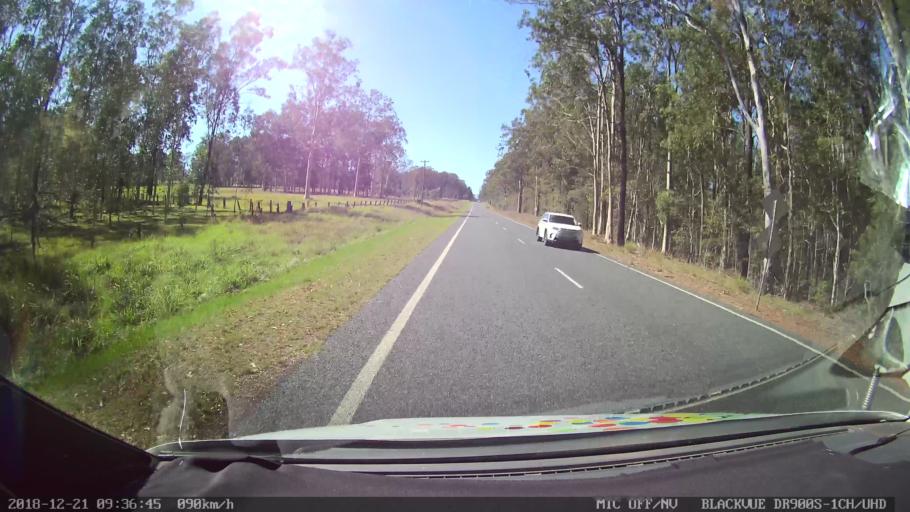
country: AU
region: New South Wales
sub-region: Clarence Valley
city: Grafton
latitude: -29.5275
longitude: 152.9843
